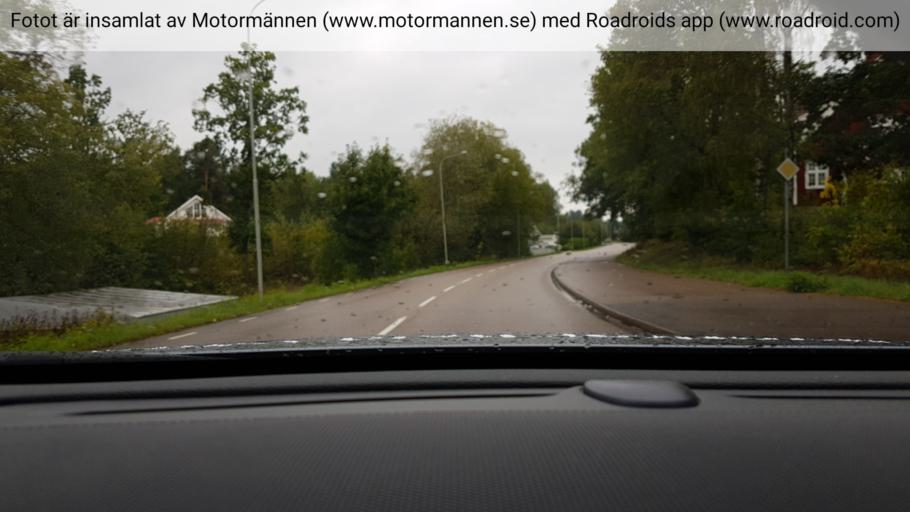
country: SE
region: Vaestra Goetaland
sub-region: Vanersborgs Kommun
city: Vargon
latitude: 58.3435
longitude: 12.3559
